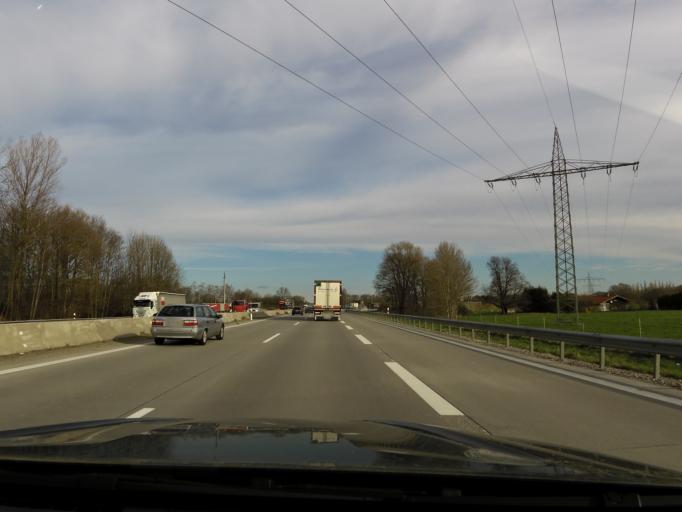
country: DE
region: Bavaria
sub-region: Upper Bavaria
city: Flintsbach
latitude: 47.7312
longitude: 12.1332
